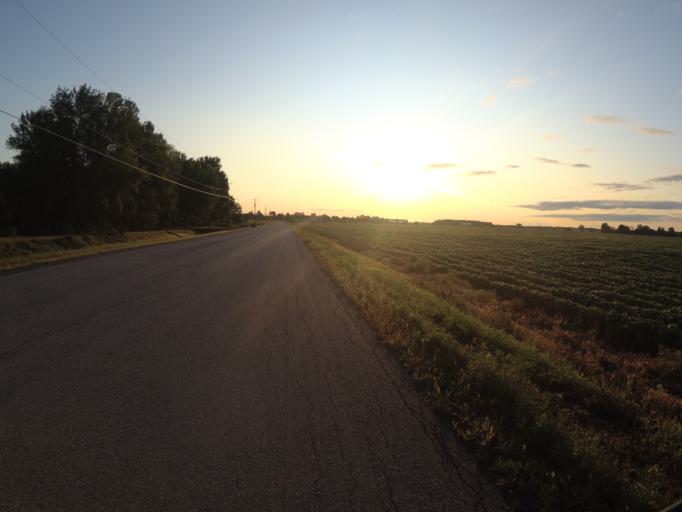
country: CA
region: Ontario
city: Ottawa
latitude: 45.1181
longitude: -75.5161
